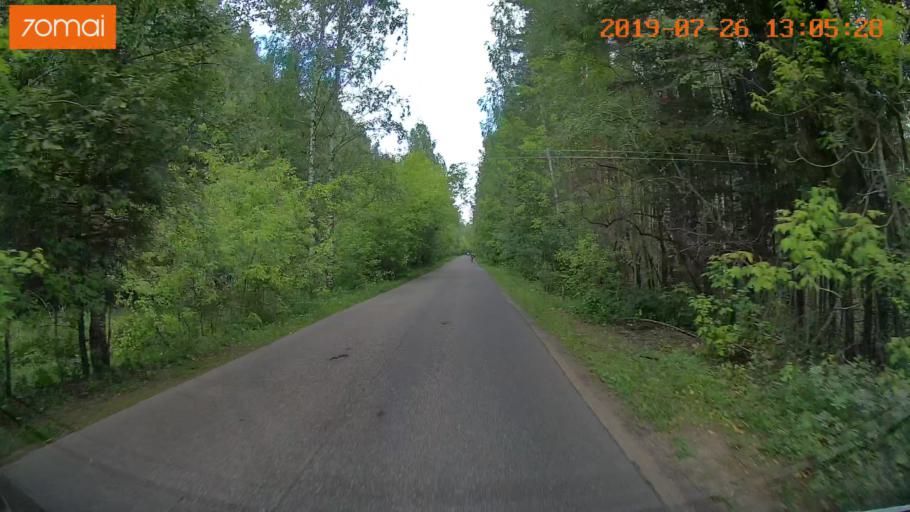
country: RU
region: Ivanovo
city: Bogorodskoye
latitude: 57.0626
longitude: 41.0356
